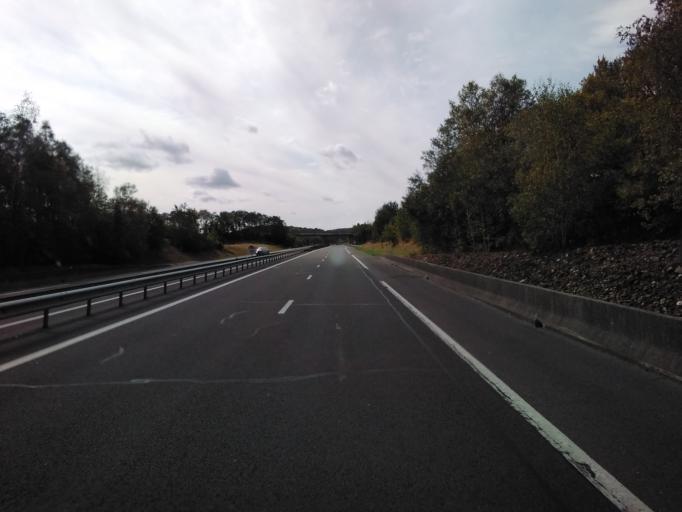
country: FR
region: Champagne-Ardenne
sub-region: Departement des Ardennes
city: Attigny
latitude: 49.6278
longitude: 4.5548
